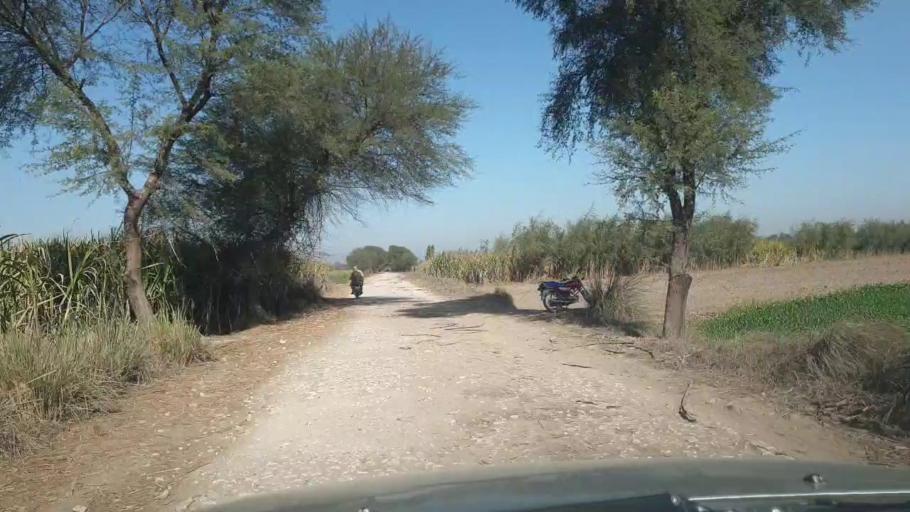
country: PK
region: Sindh
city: Ghotki
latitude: 28.0895
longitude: 69.3437
